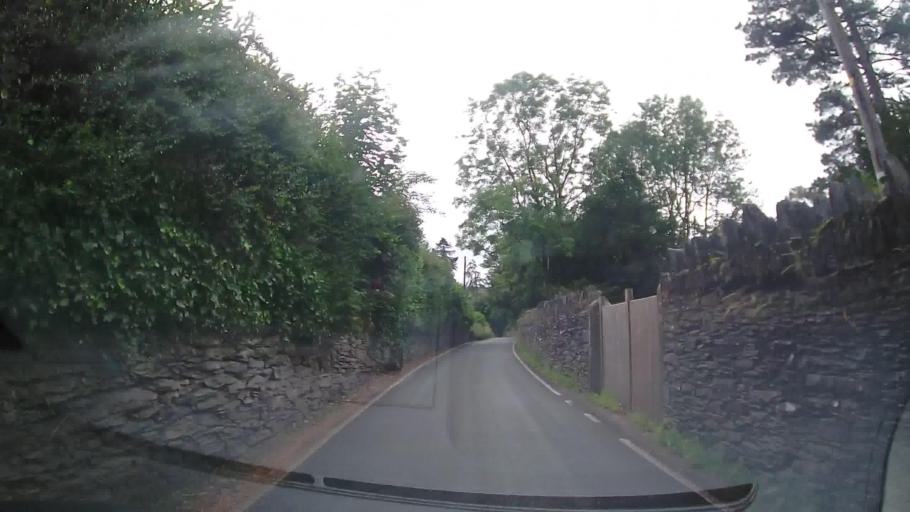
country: GB
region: Wales
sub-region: Conwy
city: Llangwm
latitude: 52.9128
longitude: -3.5134
